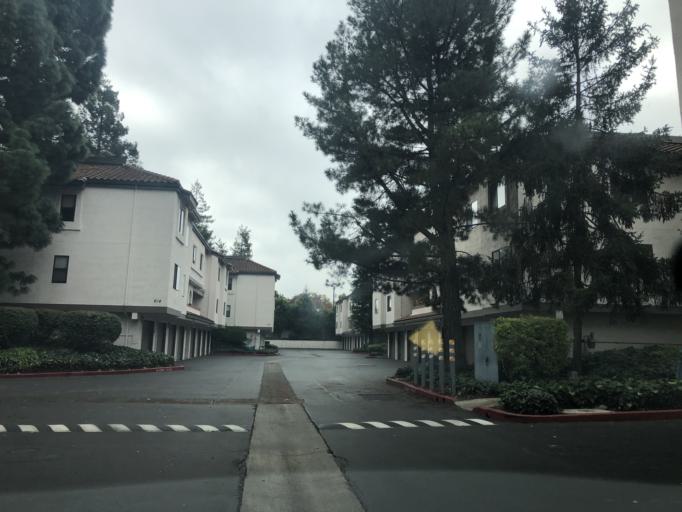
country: US
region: California
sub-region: Santa Clara County
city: Sunnyvale
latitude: 37.3922
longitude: -122.0149
